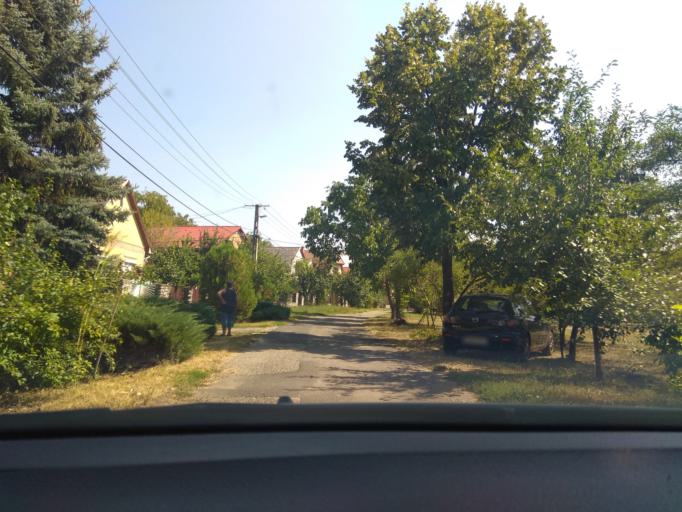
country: HU
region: Borsod-Abauj-Zemplen
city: Miskolc
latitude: 48.0730
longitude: 20.7927
